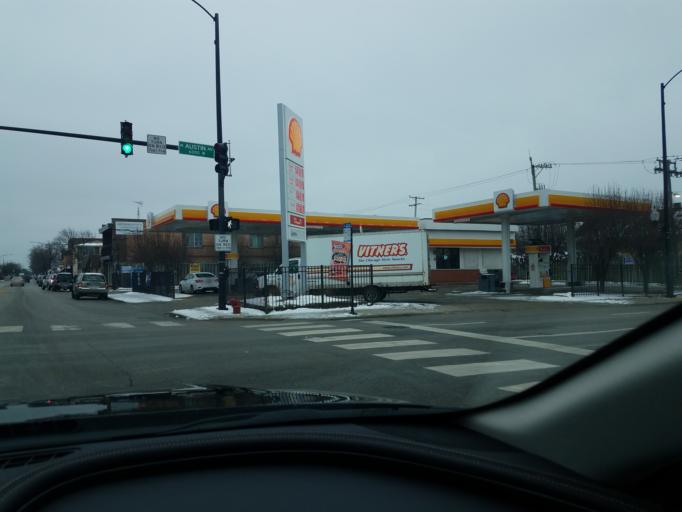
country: US
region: Illinois
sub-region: Cook County
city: Harwood Heights
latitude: 41.9603
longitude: -87.7771
